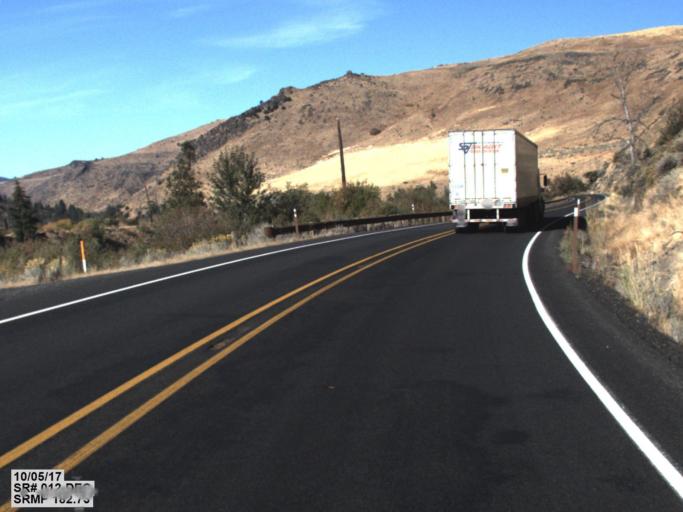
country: US
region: Washington
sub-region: Yakima County
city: Tieton
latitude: 46.7194
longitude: -120.8207
